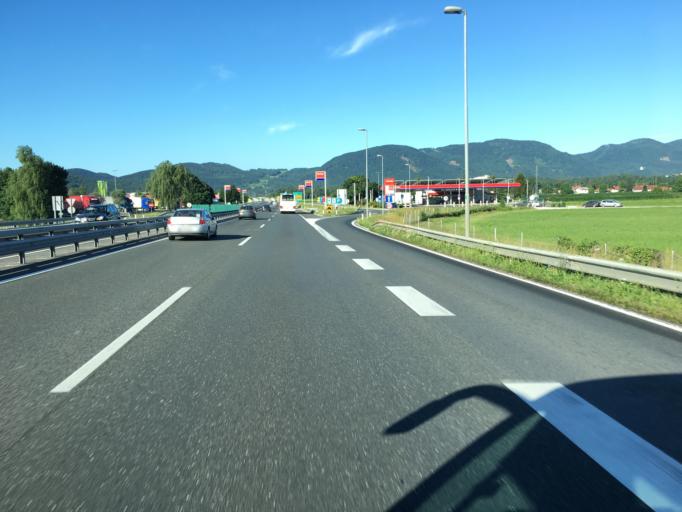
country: SI
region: Oplotnica
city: Oplotnica
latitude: 46.3500
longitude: 15.4897
